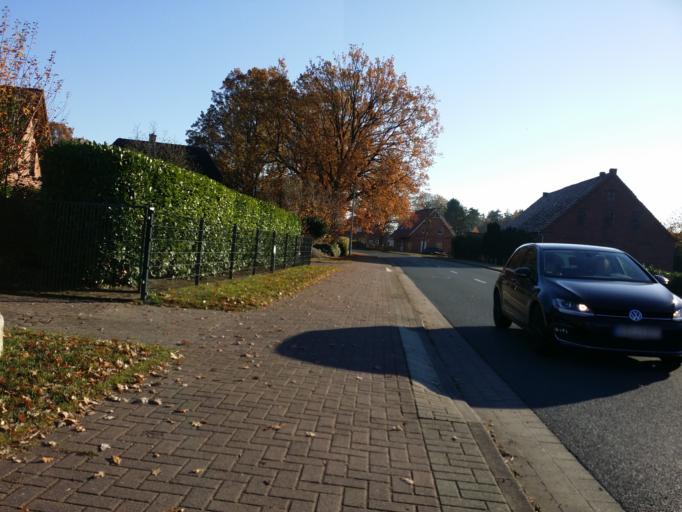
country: DE
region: Lower Saxony
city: Langwedel
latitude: 53.0320
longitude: 9.1578
